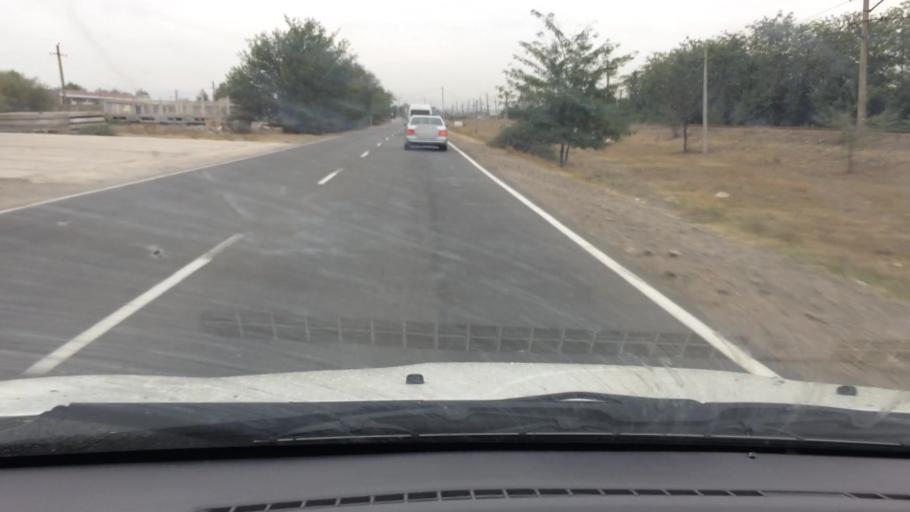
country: GE
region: Kvemo Kartli
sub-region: Marneuli
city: Marneuli
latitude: 41.4559
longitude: 44.8117
